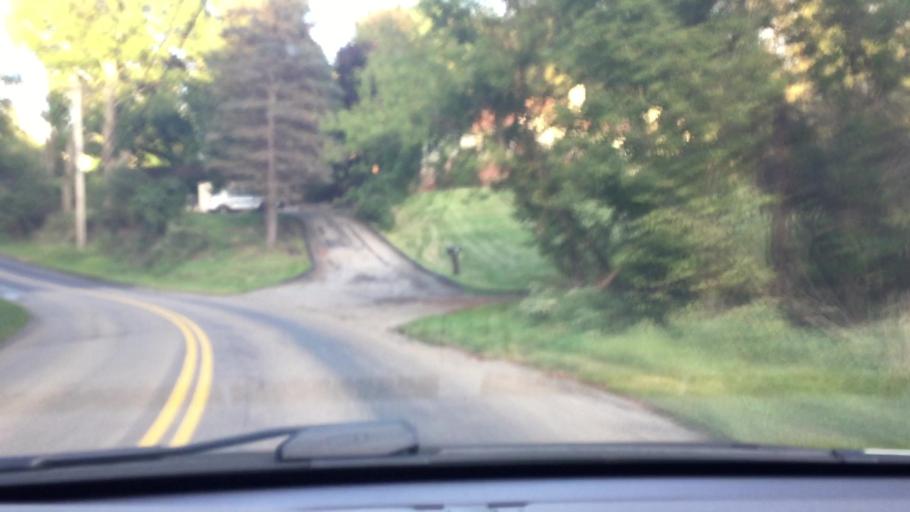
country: US
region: Pennsylvania
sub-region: Allegheny County
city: Plum
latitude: 40.4525
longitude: -79.7483
